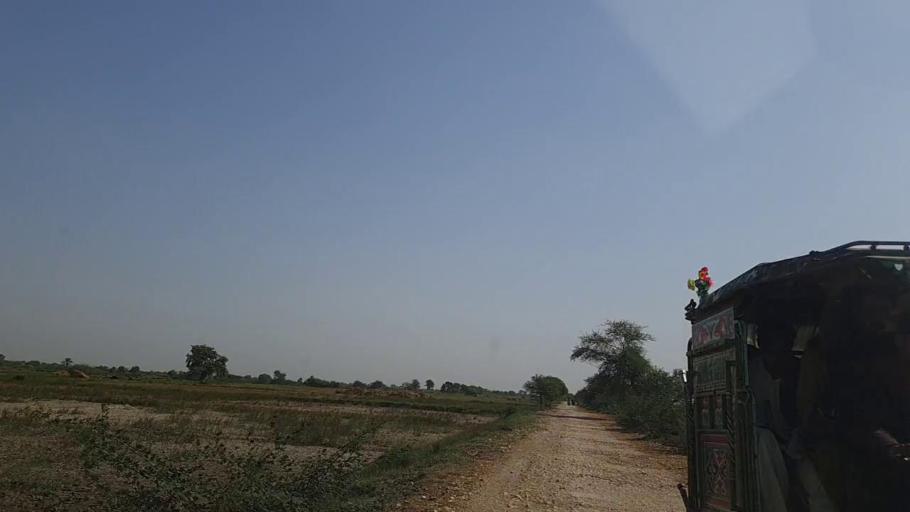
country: PK
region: Sindh
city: Daro Mehar
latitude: 24.7205
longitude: 68.0893
